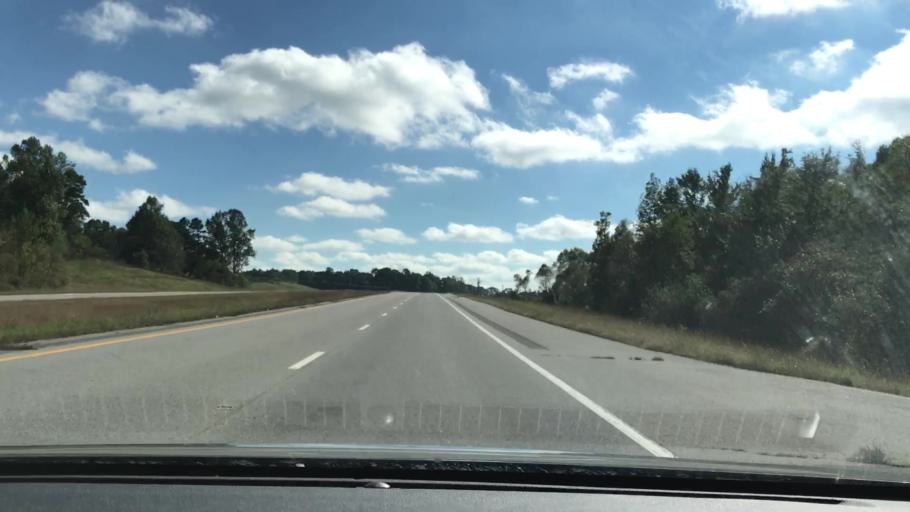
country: US
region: Tennessee
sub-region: Fentress County
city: Grimsley
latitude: 36.3252
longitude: -84.9634
